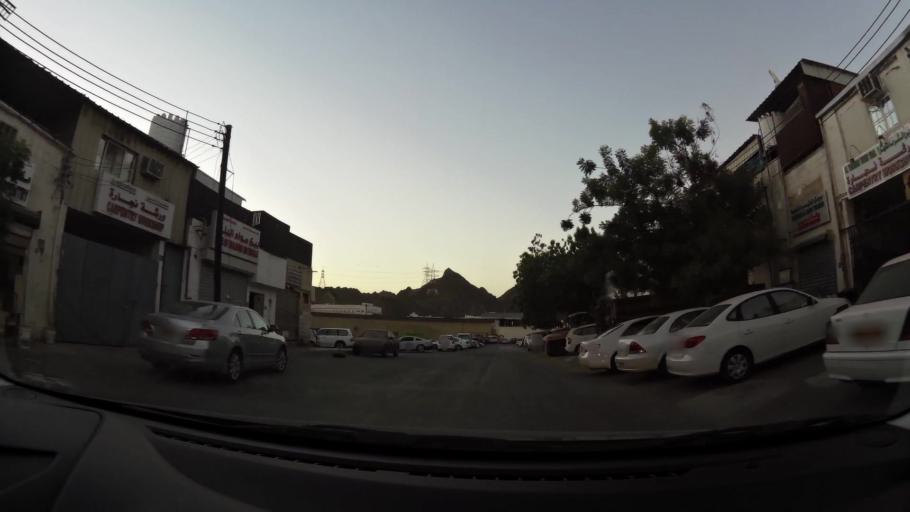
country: OM
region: Muhafazat Masqat
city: Muscat
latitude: 23.5925
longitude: 58.5644
